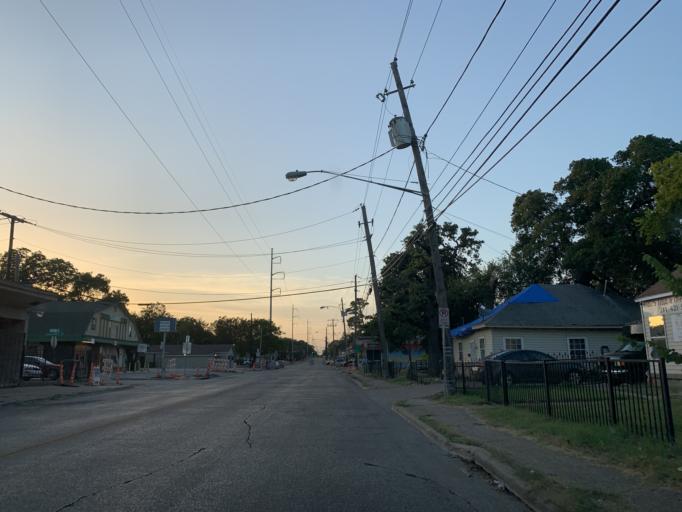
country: US
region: Texas
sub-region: Dallas County
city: Dallas
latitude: 32.7578
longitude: -96.7550
